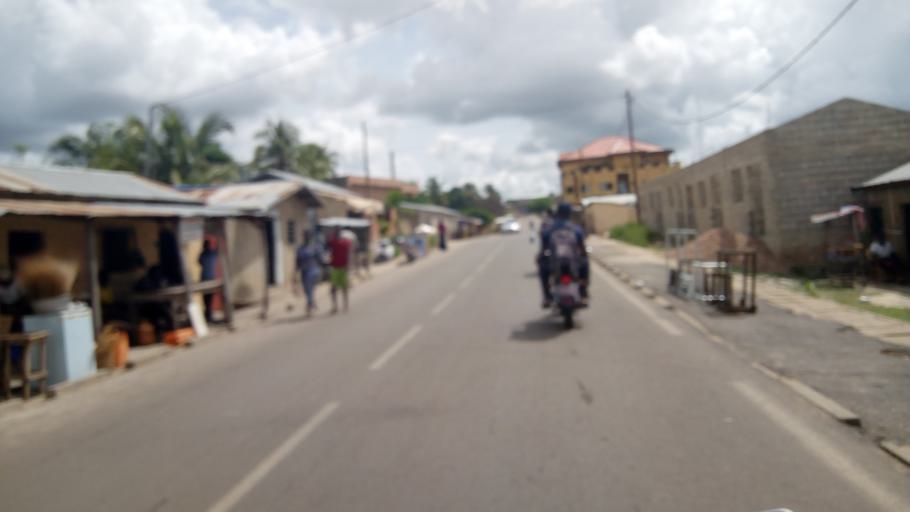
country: TG
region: Kara
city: Kara
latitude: 9.5456
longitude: 1.1869
